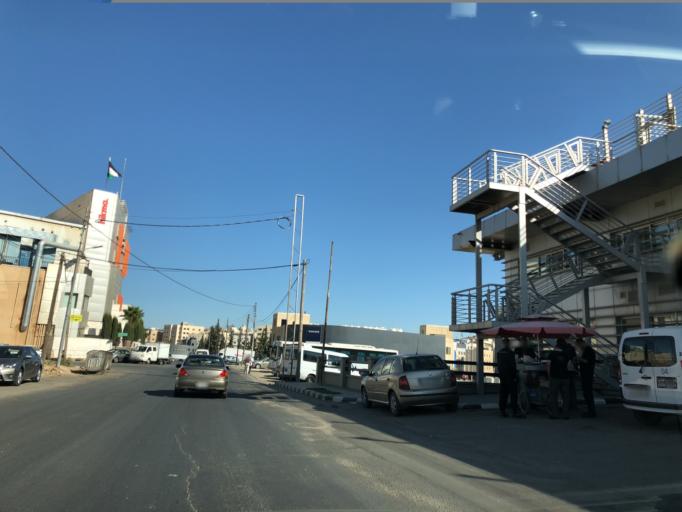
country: JO
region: Amman
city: Wadi as Sir
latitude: 31.9415
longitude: 35.8476
